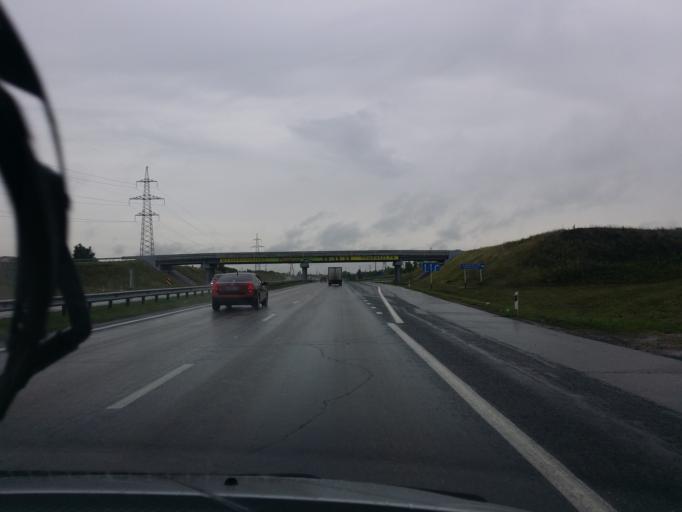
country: RU
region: Altai Krai
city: Sannikovo
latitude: 53.3398
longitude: 83.9351
